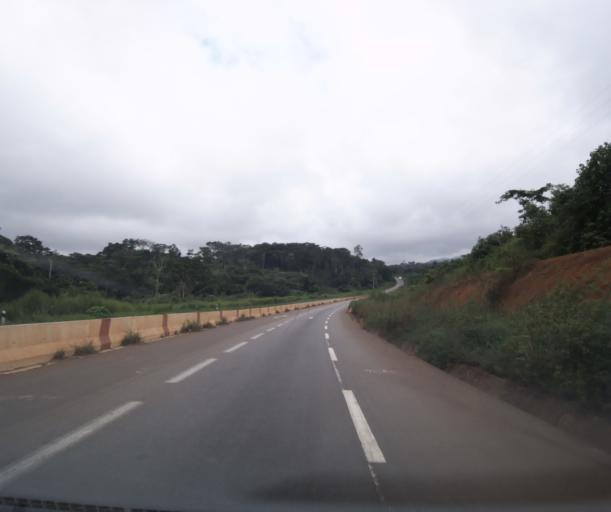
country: CM
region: Centre
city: Mbankomo
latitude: 3.7954
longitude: 11.3688
